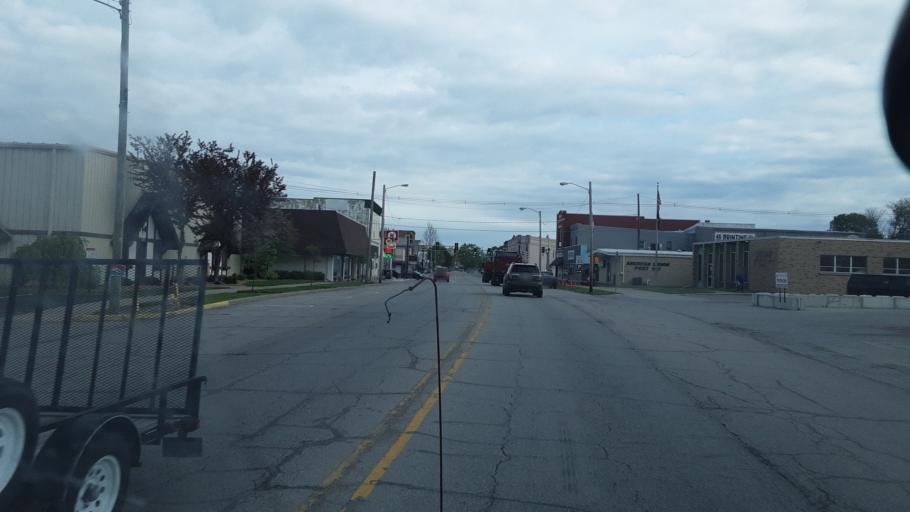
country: US
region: Indiana
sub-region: Whitley County
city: Churubusco
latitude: 41.2294
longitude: -85.3185
